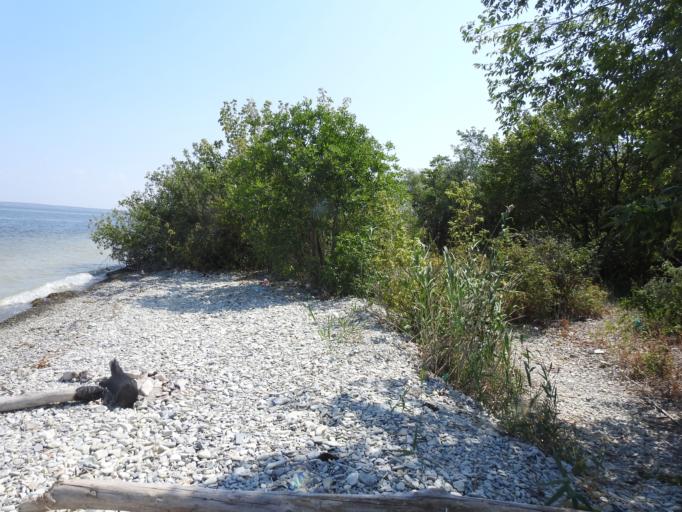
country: RU
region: Saratov
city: Kamenskiy
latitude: 50.5929
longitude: 45.6932
